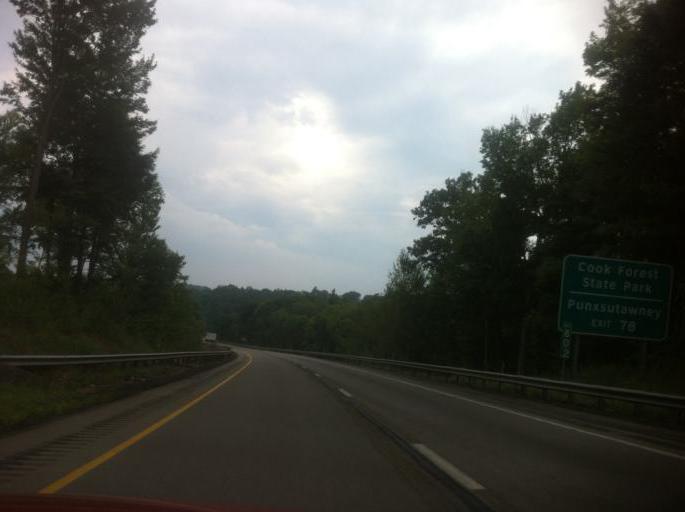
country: US
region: Pennsylvania
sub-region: Jefferson County
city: Brookville
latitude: 41.1713
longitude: -79.0665
